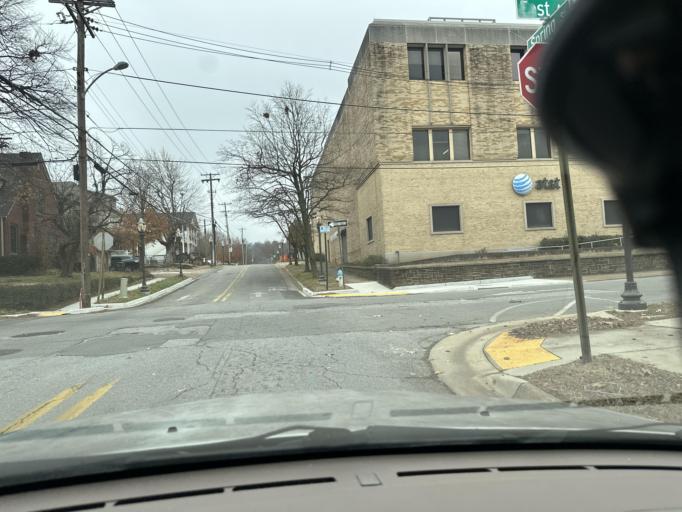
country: US
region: Arkansas
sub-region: Washington County
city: Fayetteville
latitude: 36.0647
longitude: -94.1597
